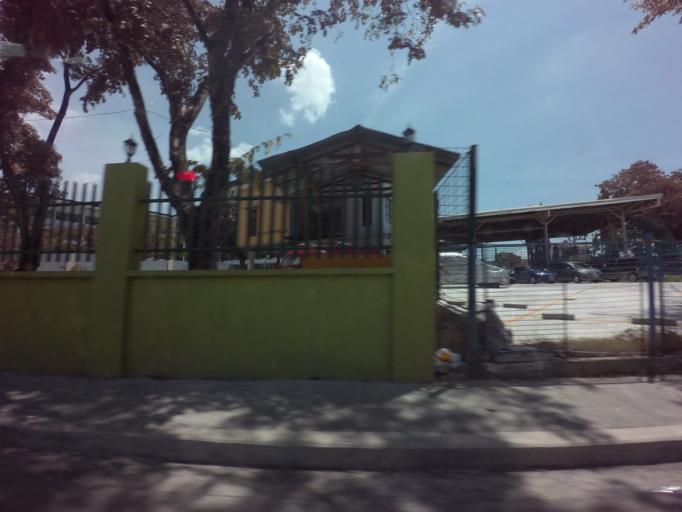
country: PH
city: Sambayanihan People's Village
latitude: 14.4229
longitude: 121.0125
